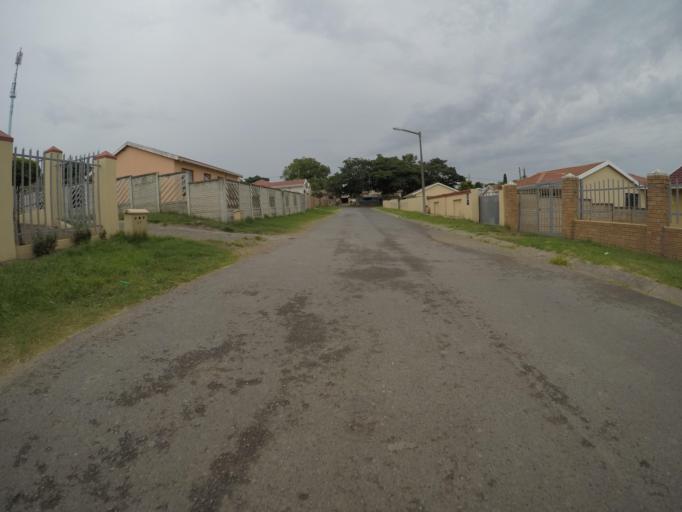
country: ZA
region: Eastern Cape
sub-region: Buffalo City Metropolitan Municipality
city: East London
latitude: -32.9686
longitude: 27.8328
